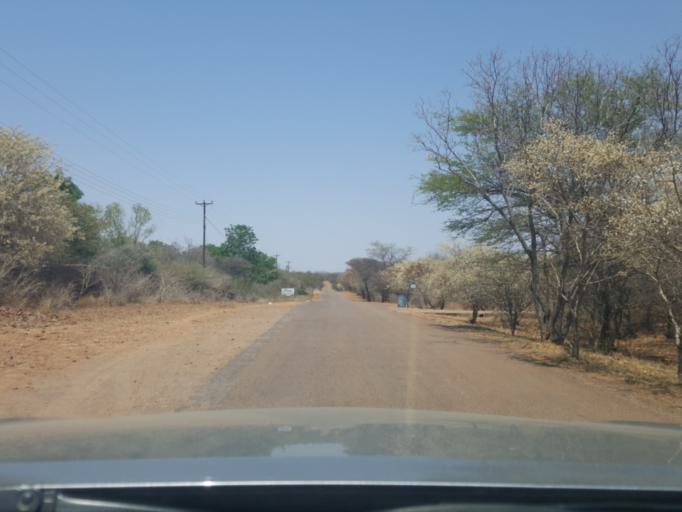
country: BW
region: South East
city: Ramotswa
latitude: -24.7655
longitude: 25.8454
